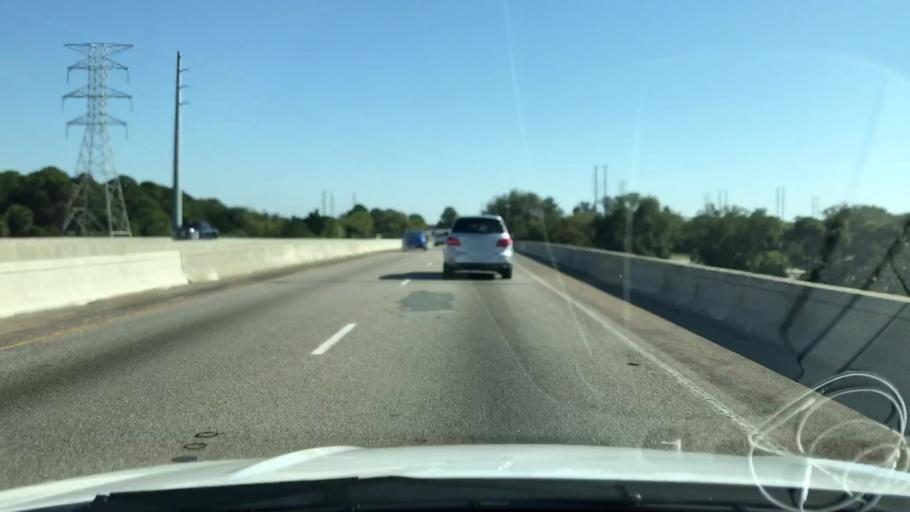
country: US
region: South Carolina
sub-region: Beaufort County
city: Hilton Head Island
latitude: 32.2295
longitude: -80.7889
